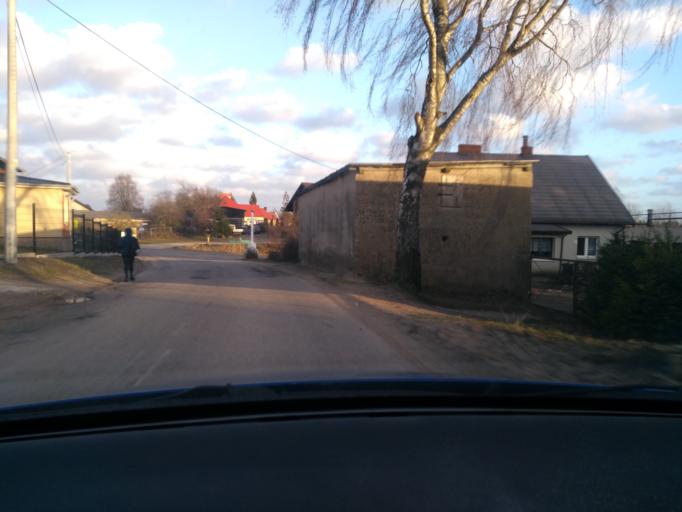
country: PL
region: Pomeranian Voivodeship
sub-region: Powiat kartuski
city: Przodkowo
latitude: 54.4143
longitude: 18.3121
